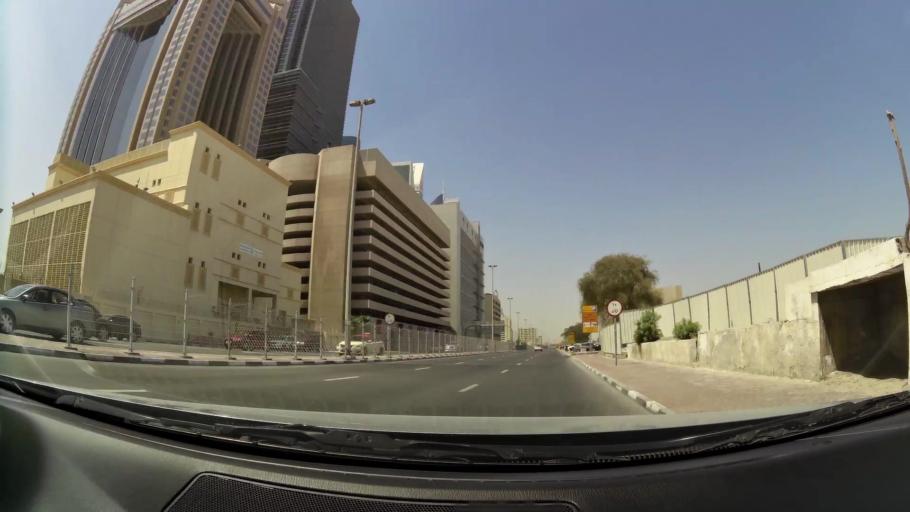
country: AE
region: Ash Shariqah
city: Sharjah
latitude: 25.2279
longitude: 55.2835
